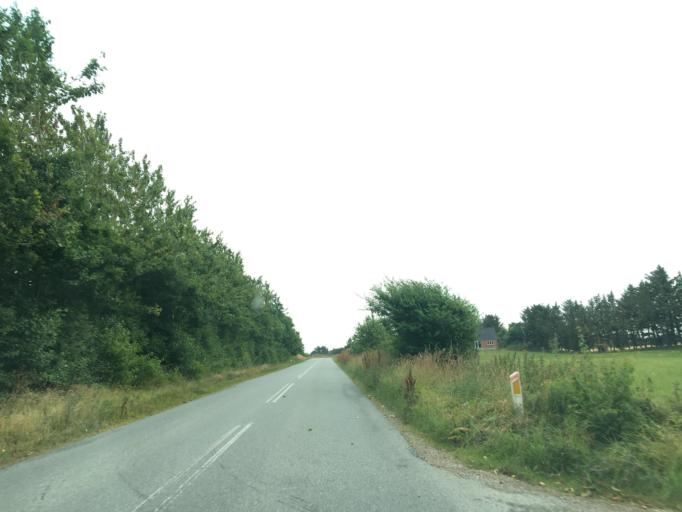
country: DK
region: North Denmark
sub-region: Thisted Kommune
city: Hurup
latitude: 56.7970
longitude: 8.4124
